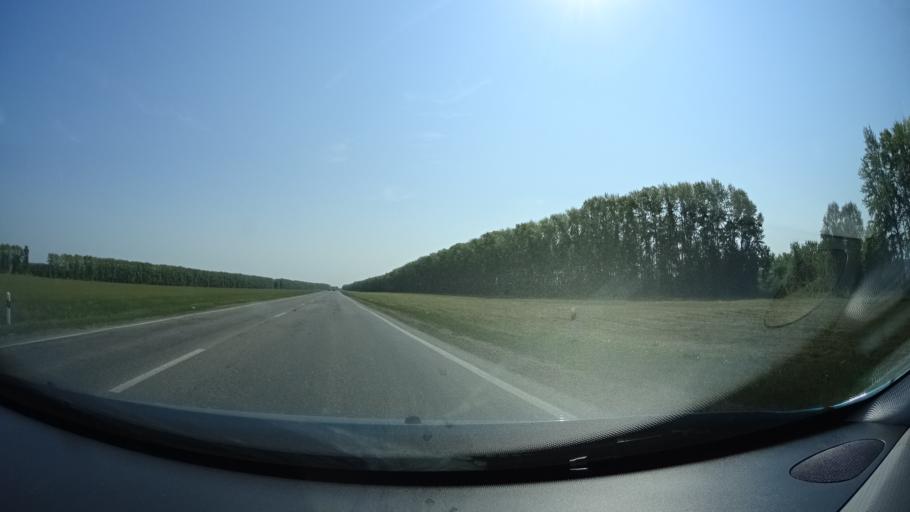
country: RU
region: Bashkortostan
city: Karmaskaly
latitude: 54.3982
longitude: 56.1004
